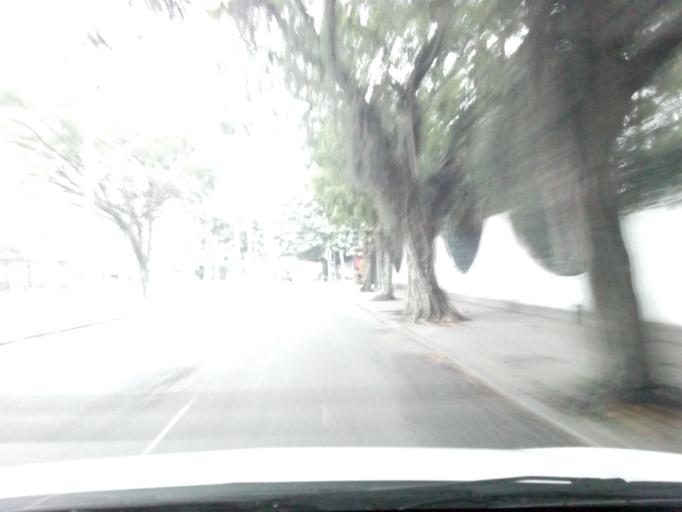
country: BR
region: Rio de Janeiro
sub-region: Rio De Janeiro
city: Rio de Janeiro
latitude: -22.9516
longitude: -43.1743
